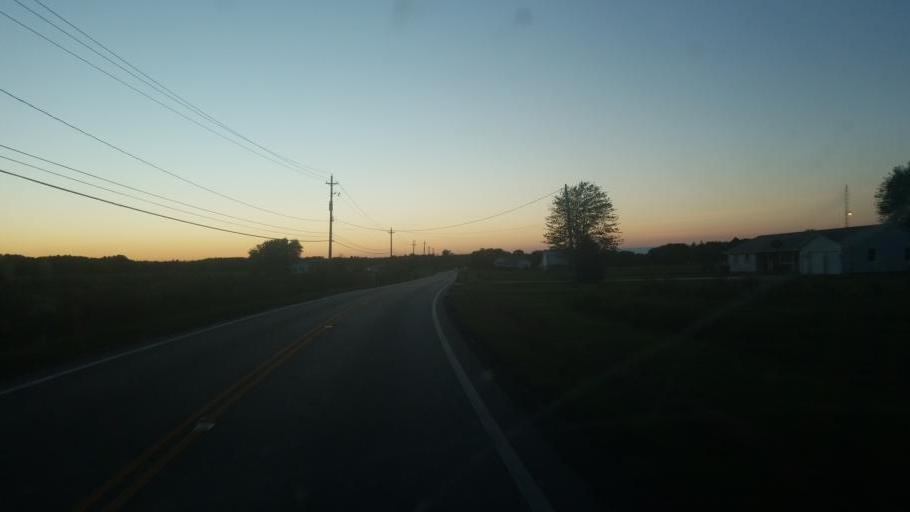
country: US
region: Ohio
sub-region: Ashtabula County
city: Andover
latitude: 41.7513
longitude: -80.6037
